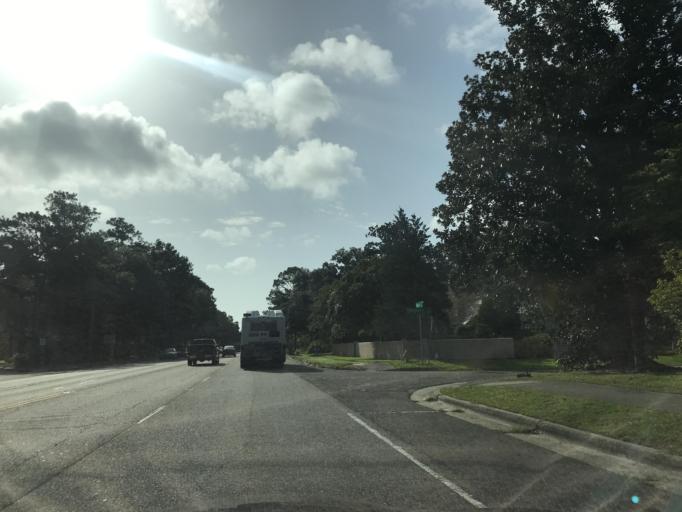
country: US
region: North Carolina
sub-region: New Hanover County
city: Wilmington
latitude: 34.2204
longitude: -77.9136
